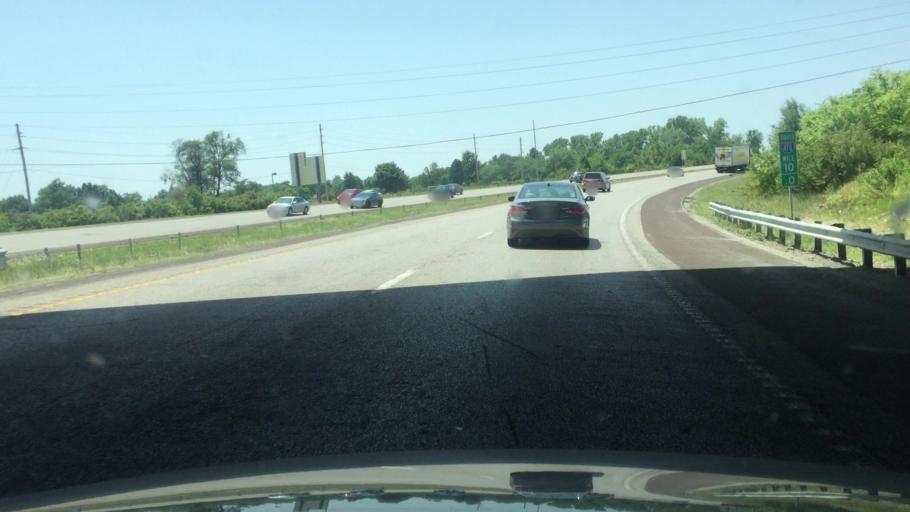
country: US
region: Missouri
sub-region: Jackson County
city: Lees Summit
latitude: 38.9462
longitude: -94.3648
